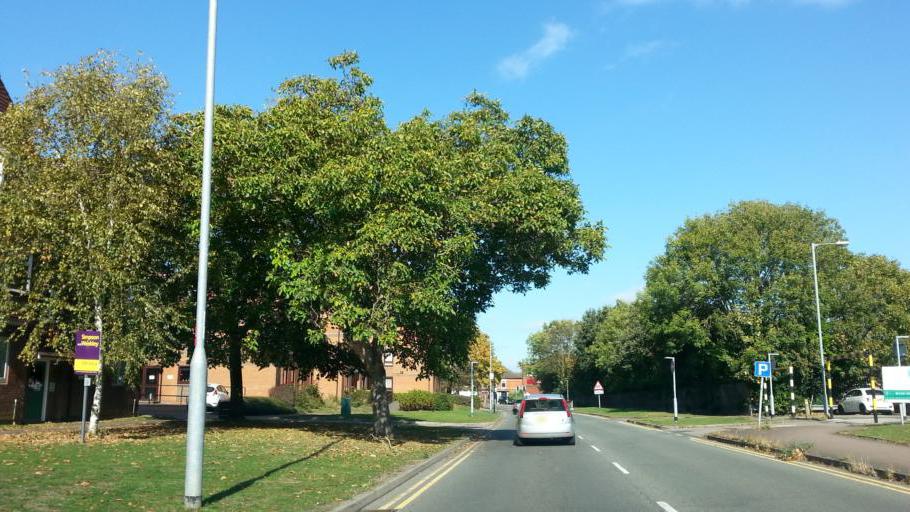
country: GB
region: England
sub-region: Northamptonshire
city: Rushden
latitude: 52.2895
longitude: -0.6003
